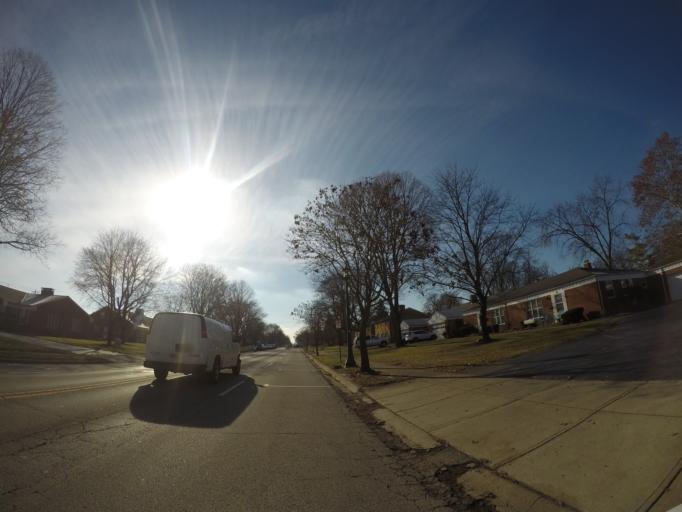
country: US
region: Ohio
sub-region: Franklin County
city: Upper Arlington
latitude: 40.0160
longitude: -83.0577
